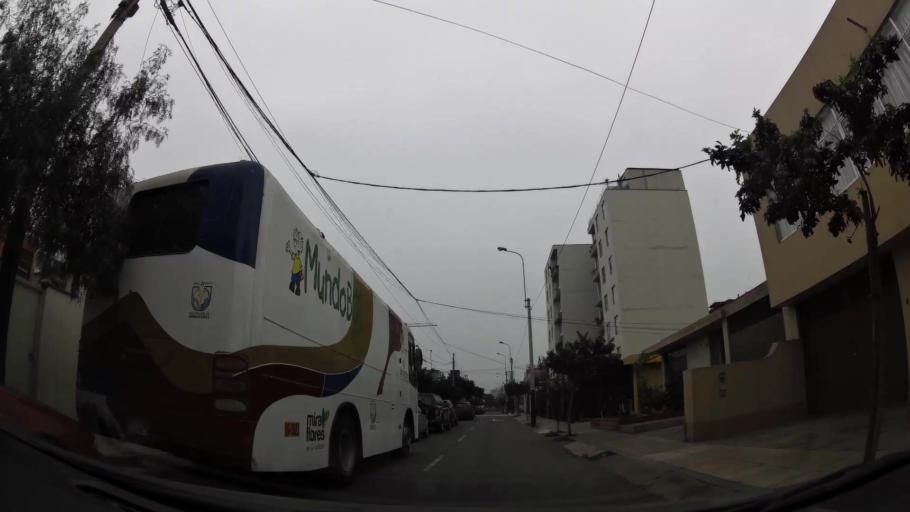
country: PE
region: Lima
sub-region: Lima
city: San Isidro
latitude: -12.1114
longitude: -77.0496
